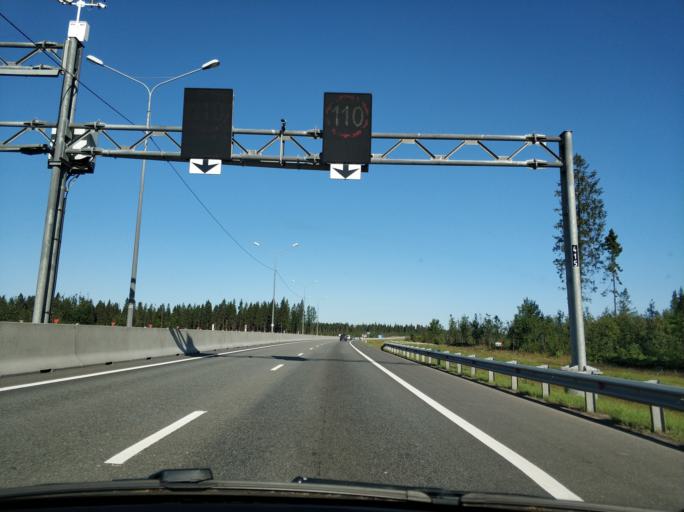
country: RU
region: Leningrad
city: Sosnovo
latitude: 60.4364
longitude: 30.2255
